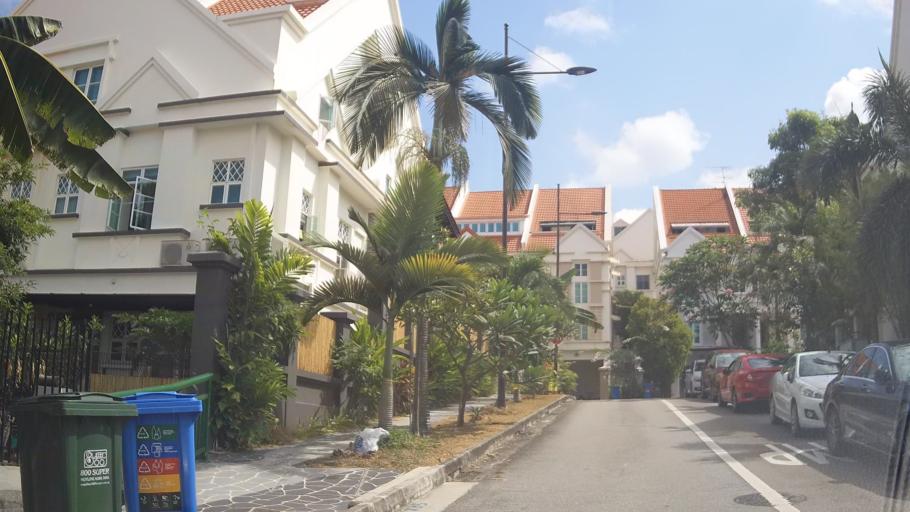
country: SG
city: Singapore
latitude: 1.3239
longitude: 103.9492
